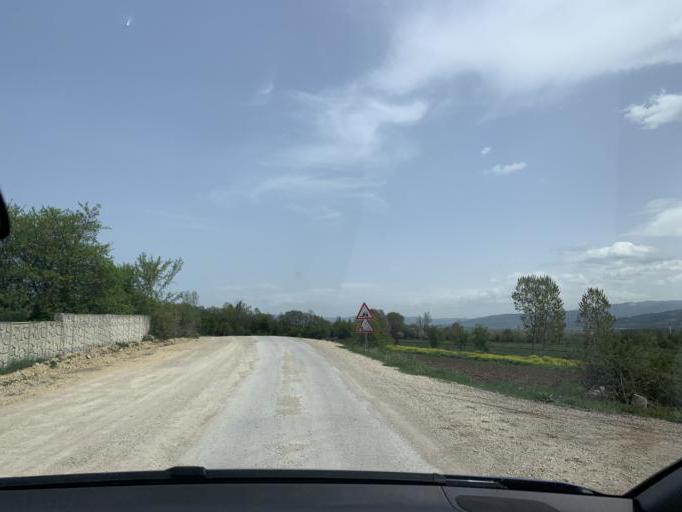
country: TR
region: Bolu
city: Bolu
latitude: 40.7599
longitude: 31.6937
